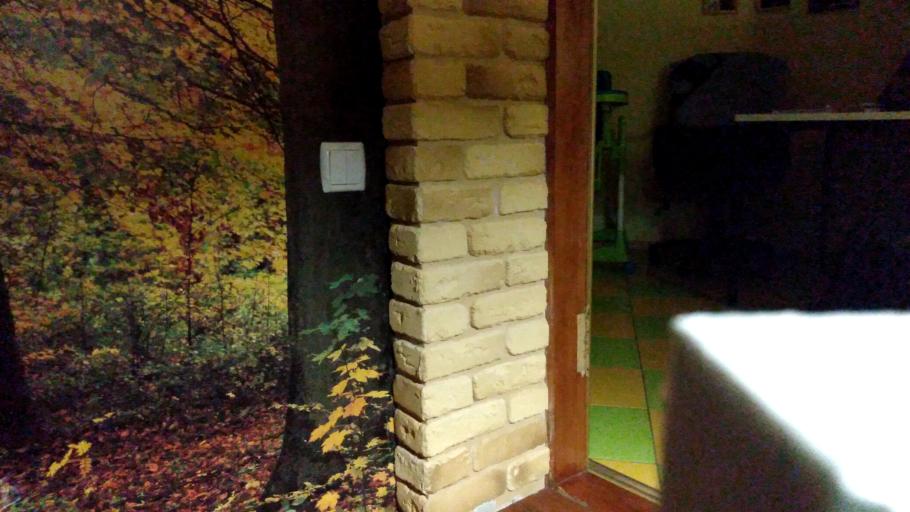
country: RU
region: Vologda
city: Lipin Bor
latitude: 61.1368
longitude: 37.9114
